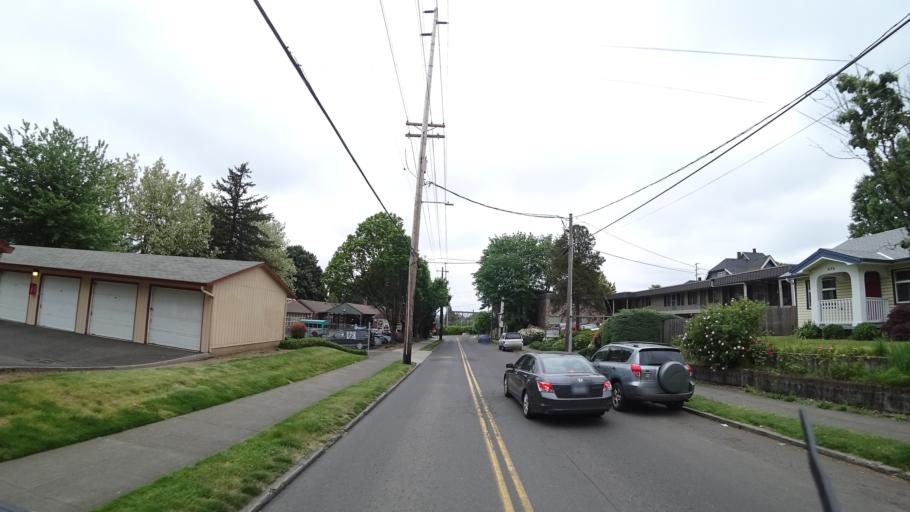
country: US
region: Oregon
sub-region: Multnomah County
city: Lents
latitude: 45.5183
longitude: -122.6021
